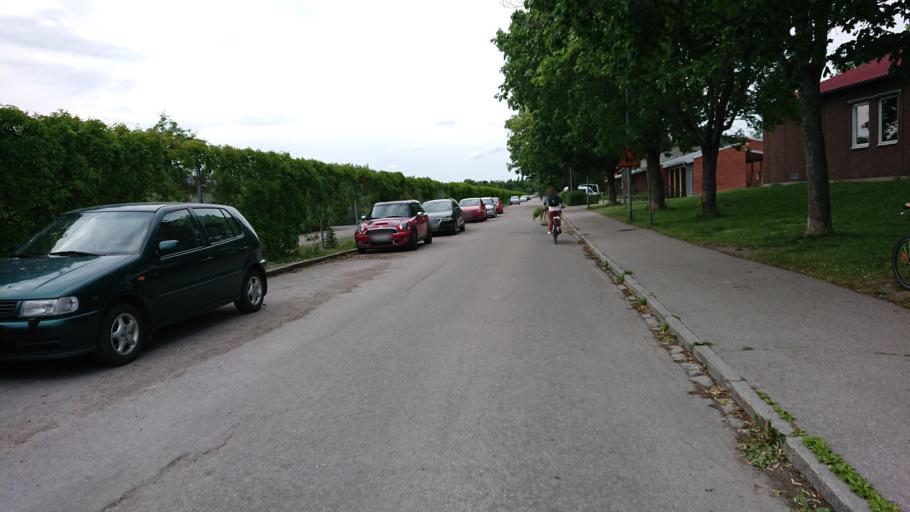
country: SE
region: Uppsala
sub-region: Uppsala Kommun
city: Uppsala
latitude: 59.8745
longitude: 17.6160
